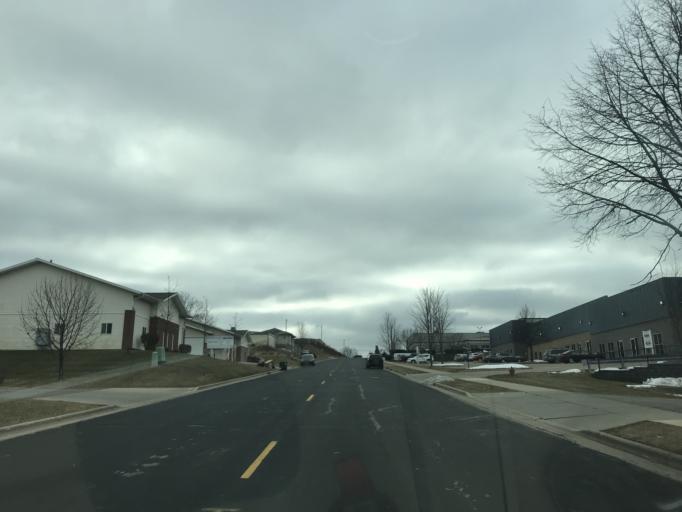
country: US
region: Wisconsin
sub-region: Dane County
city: Monona
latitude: 43.1092
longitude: -89.3100
